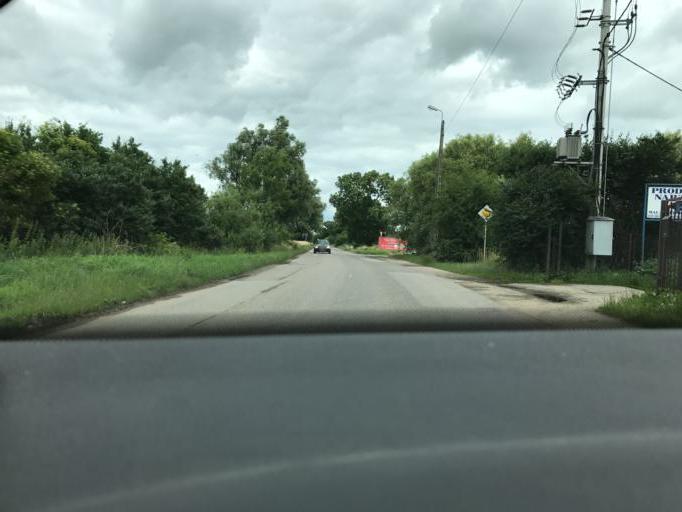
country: PL
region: Pomeranian Voivodeship
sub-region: Powiat gdanski
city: Pruszcz Gdanski
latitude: 54.2749
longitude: 18.6931
